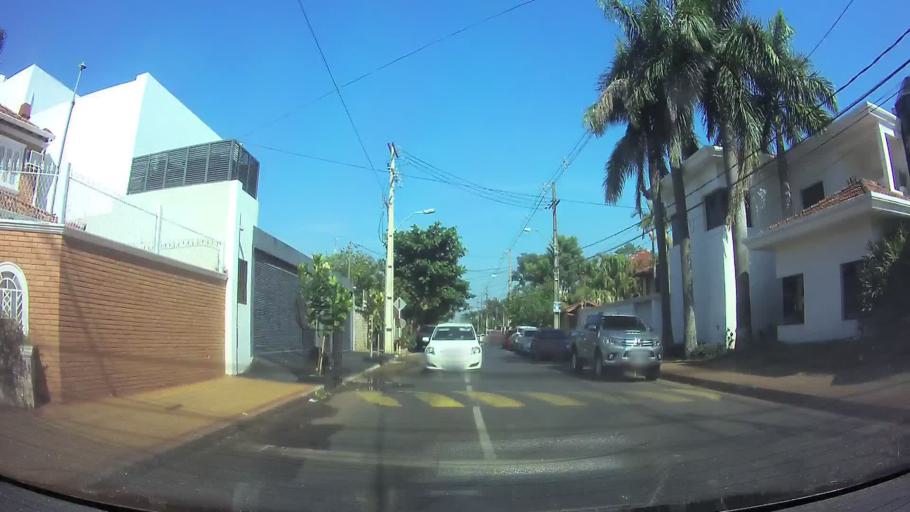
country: PY
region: Central
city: Fernando de la Mora
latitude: -25.2900
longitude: -57.5676
